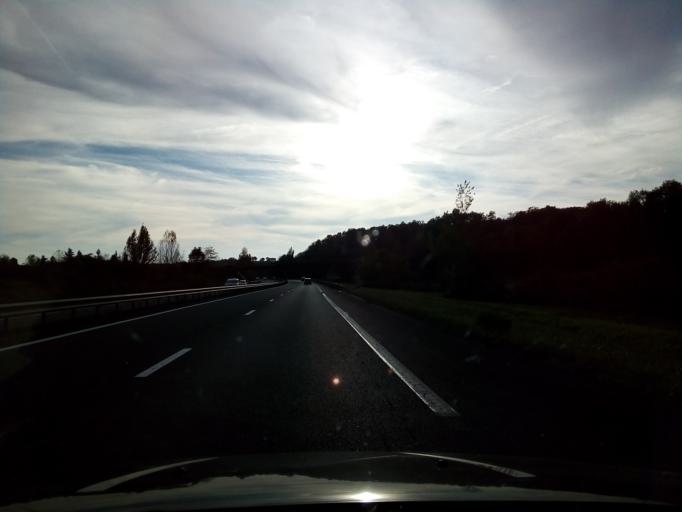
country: FR
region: Poitou-Charentes
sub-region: Departement de la Charente
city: Taponnat-Fleurignac
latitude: 45.7854
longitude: 0.4120
